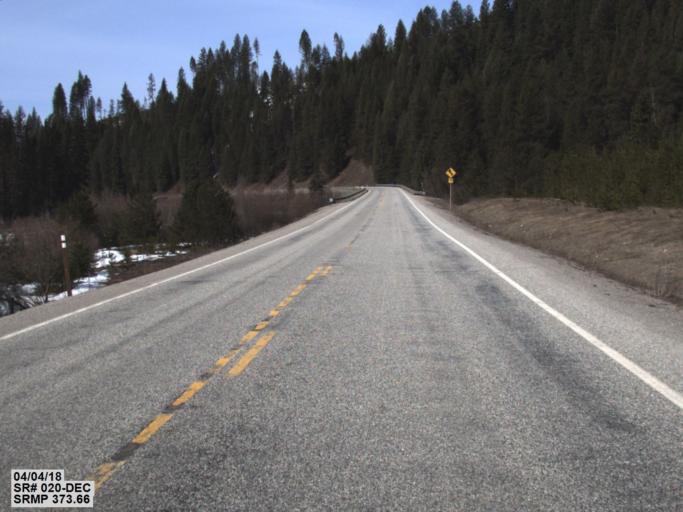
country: US
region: Washington
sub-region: Stevens County
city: Chewelah
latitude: 48.5445
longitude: -117.5819
